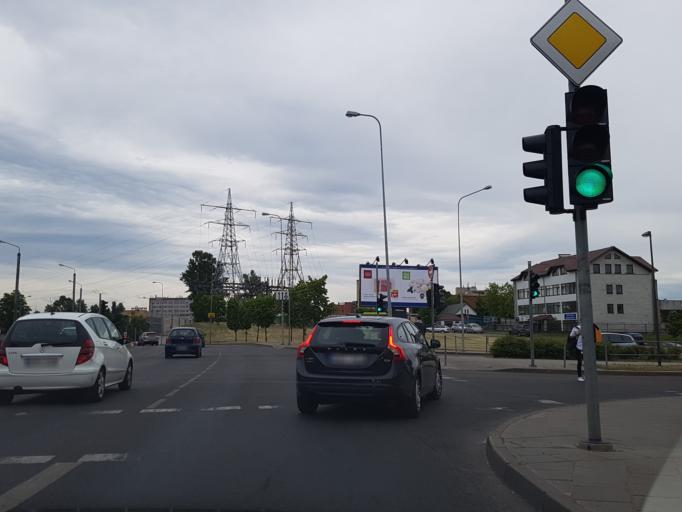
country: LT
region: Vilnius County
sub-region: Vilnius
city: Vilnius
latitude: 54.7175
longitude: 25.2863
